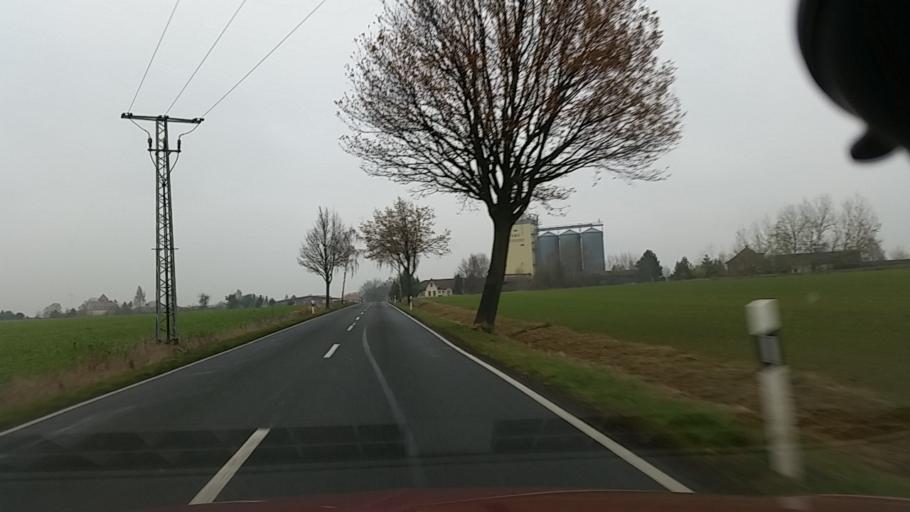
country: DE
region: Lower Saxony
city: Wittingen
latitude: 52.6896
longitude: 10.8075
